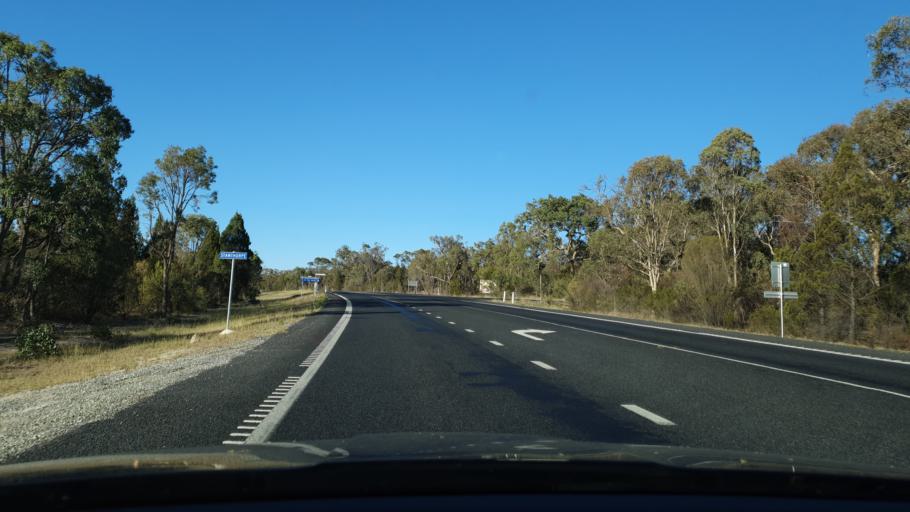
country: AU
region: Queensland
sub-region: Southern Downs
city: Stanthorpe
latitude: -28.6811
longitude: 151.9197
